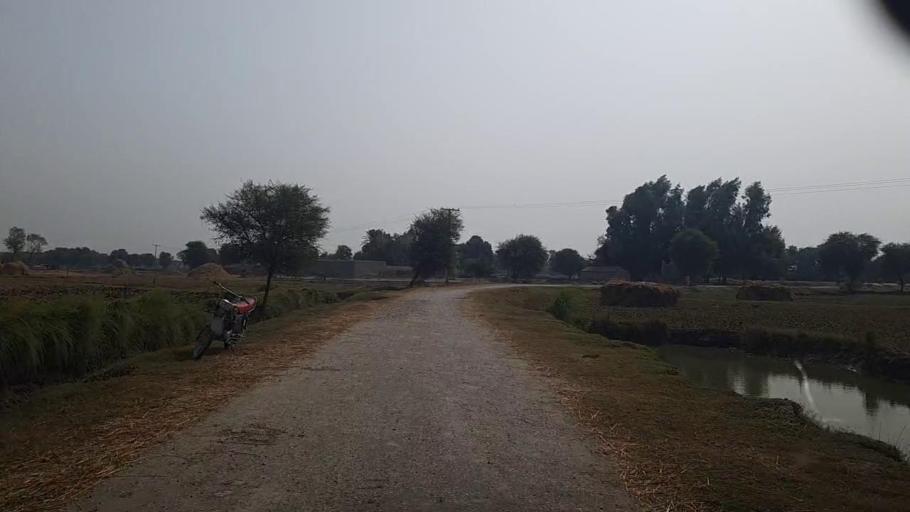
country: PK
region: Sindh
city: Kashmor
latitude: 28.3797
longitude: 69.4457
